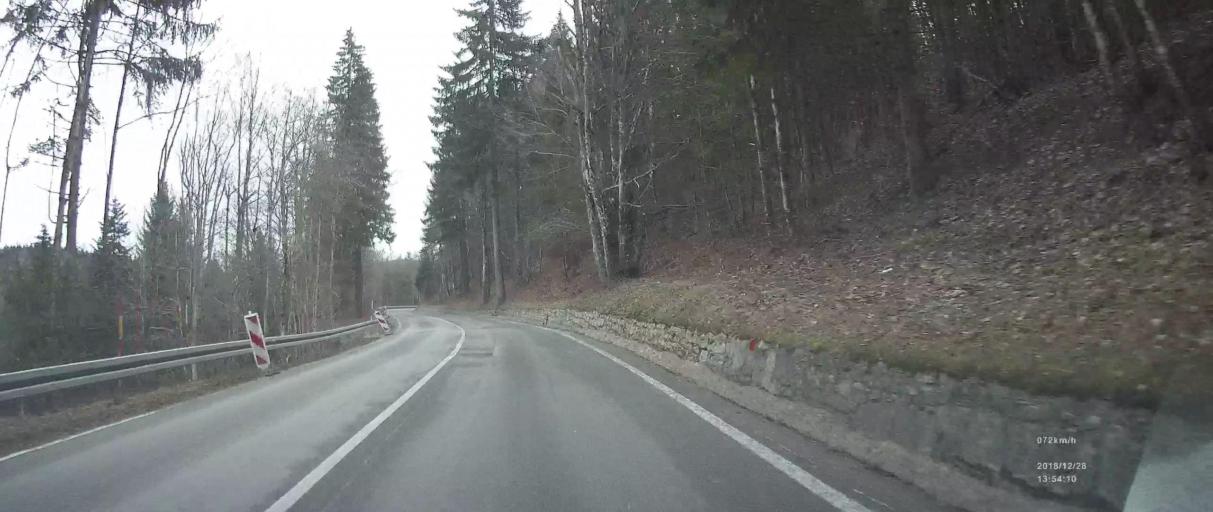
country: HR
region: Primorsko-Goranska
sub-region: Grad Delnice
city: Delnice
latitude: 45.3877
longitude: 14.8605
